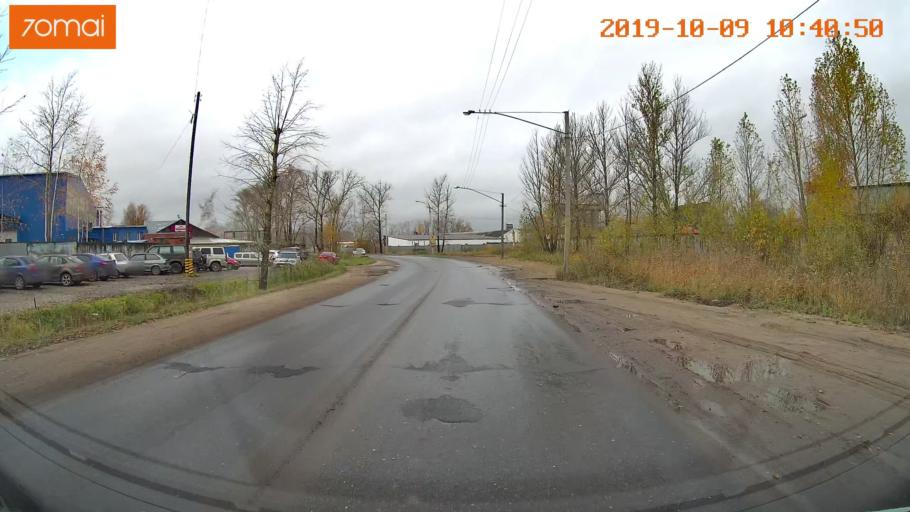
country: RU
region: Vologda
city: Vologda
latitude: 59.2341
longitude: 39.8344
